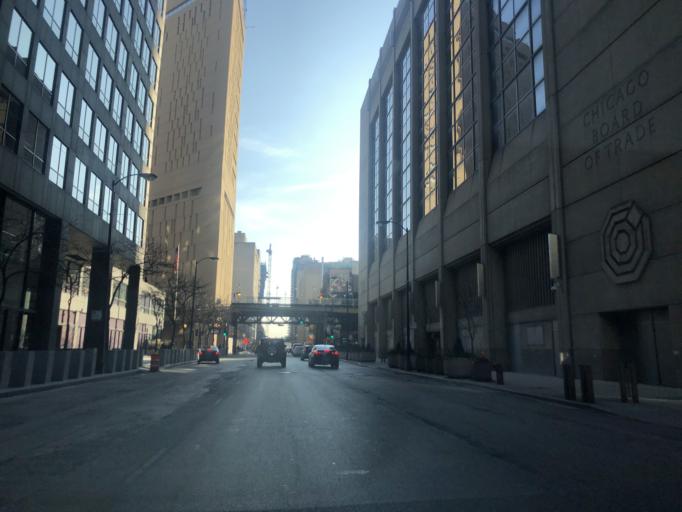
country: US
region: Illinois
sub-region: Cook County
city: Chicago
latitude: 41.8779
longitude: -87.6308
